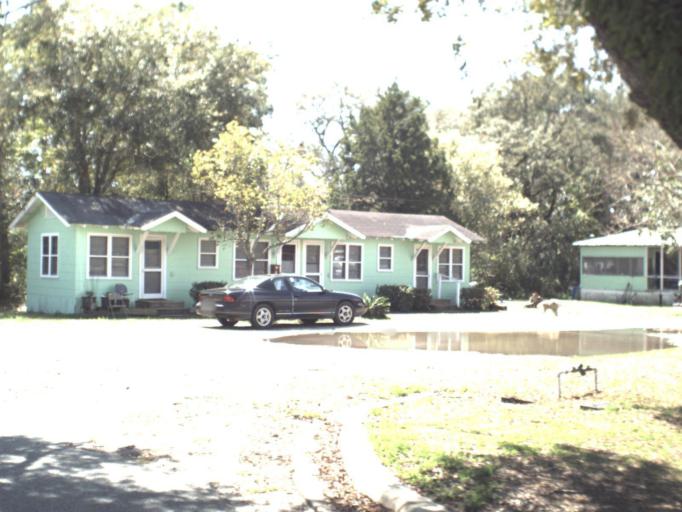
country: US
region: Florida
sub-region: Wakulla County
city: Crawfordville
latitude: 30.0319
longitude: -84.3905
